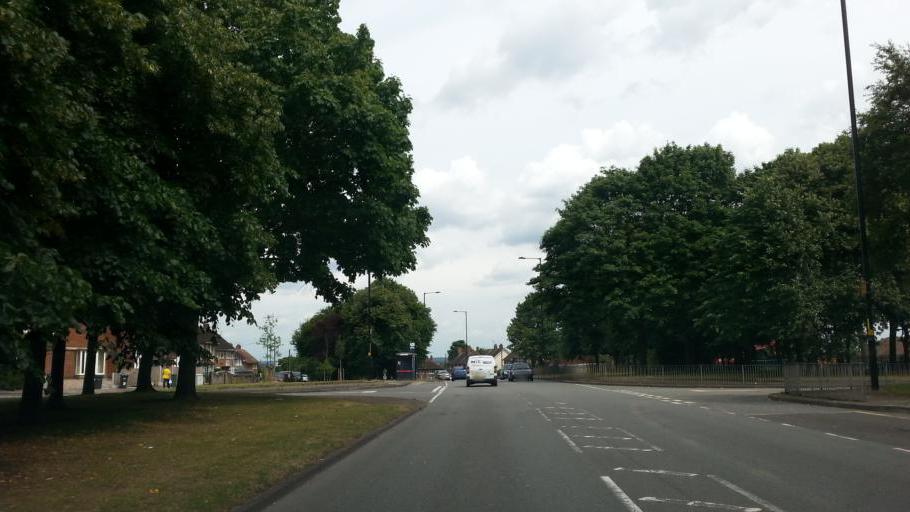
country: GB
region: England
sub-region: City and Borough of Birmingham
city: Acocks Green
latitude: 52.4773
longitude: -1.7868
